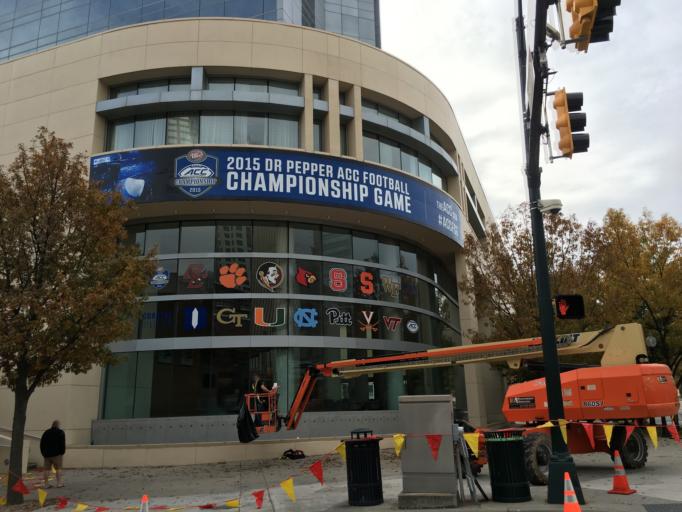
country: US
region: North Carolina
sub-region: Mecklenburg County
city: Charlotte
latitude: 35.2224
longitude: -80.8474
